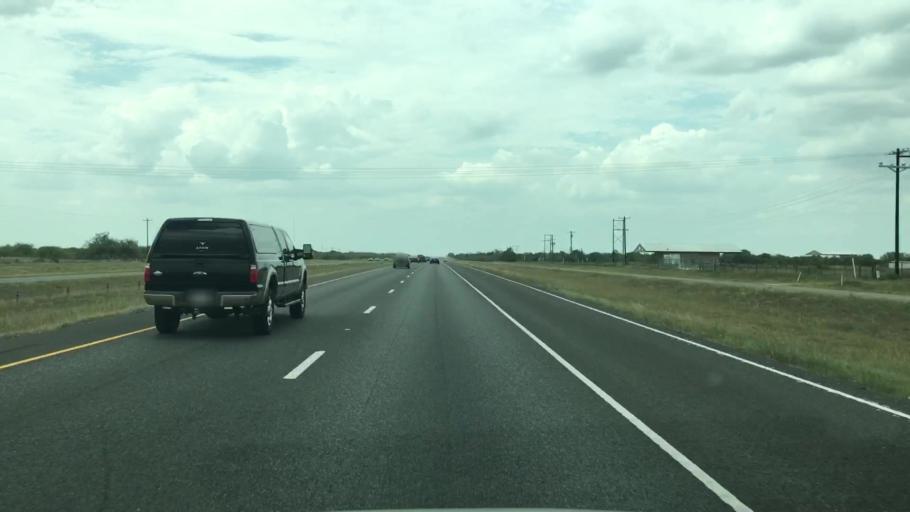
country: US
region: Texas
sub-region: Atascosa County
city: Pleasanton
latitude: 28.7981
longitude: -98.3408
